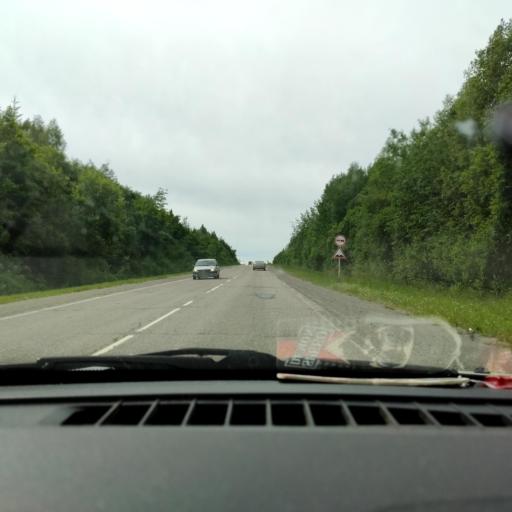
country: RU
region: Perm
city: Chusovoy
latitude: 58.3742
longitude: 57.9709
